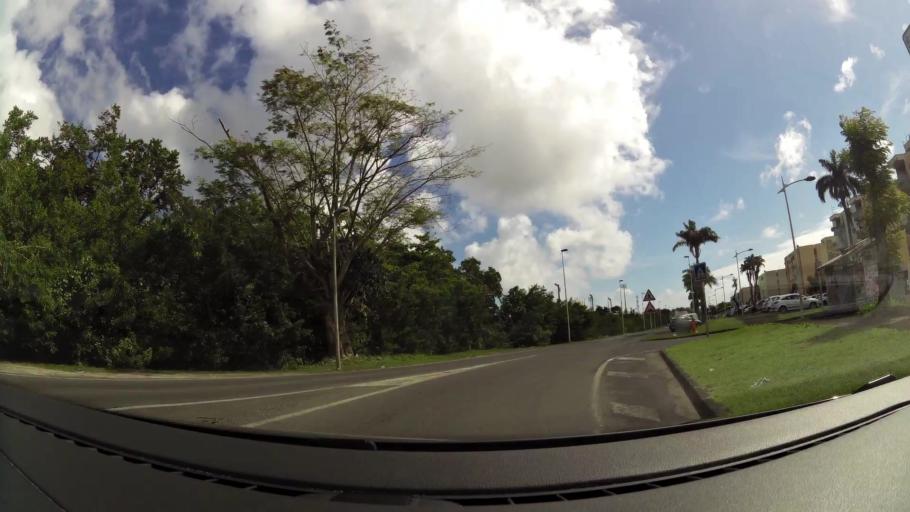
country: GP
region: Guadeloupe
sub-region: Guadeloupe
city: Pointe-a-Pitre
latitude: 16.2520
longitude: -61.5464
